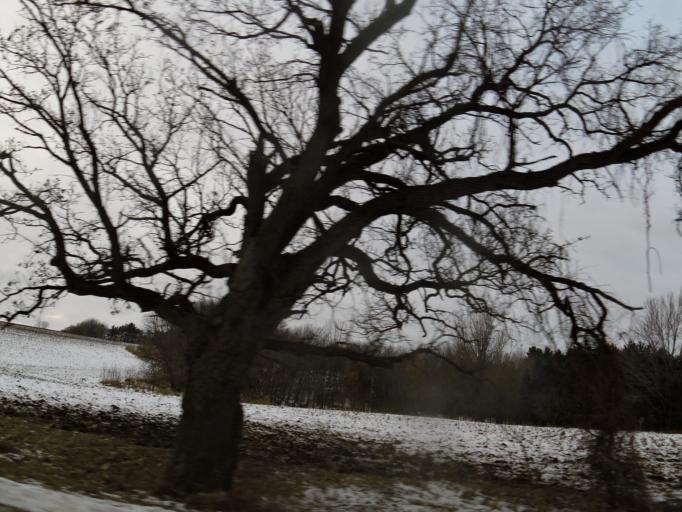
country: US
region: Minnesota
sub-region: Carver County
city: Carver
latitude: 44.7448
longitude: -93.6553
